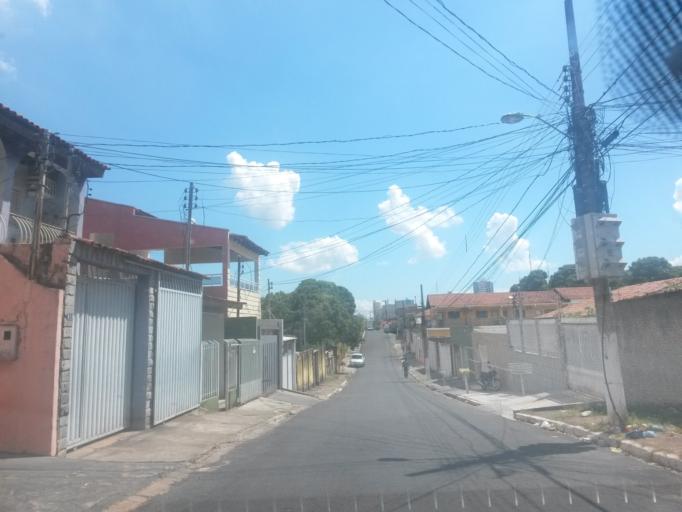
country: BR
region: Mato Grosso
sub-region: Cuiaba
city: Cuiaba
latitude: -15.5960
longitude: -56.0881
